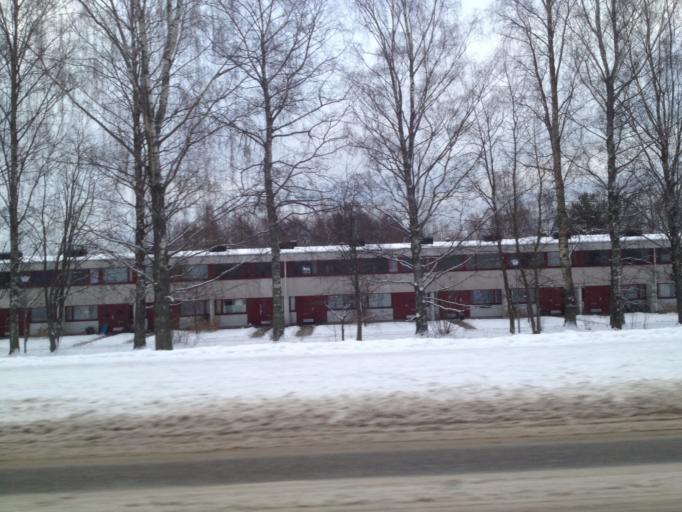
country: FI
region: Uusimaa
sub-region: Helsinki
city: Vantaa
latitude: 60.2210
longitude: 25.1468
